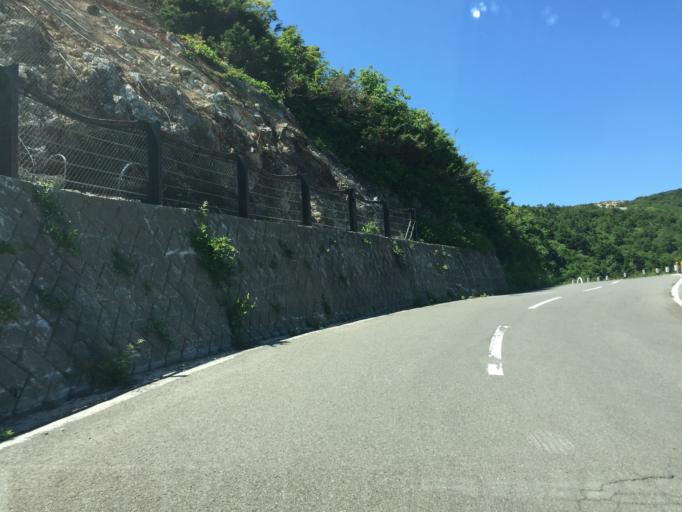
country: JP
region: Fukushima
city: Fukushima-shi
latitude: 37.7366
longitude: 140.2687
